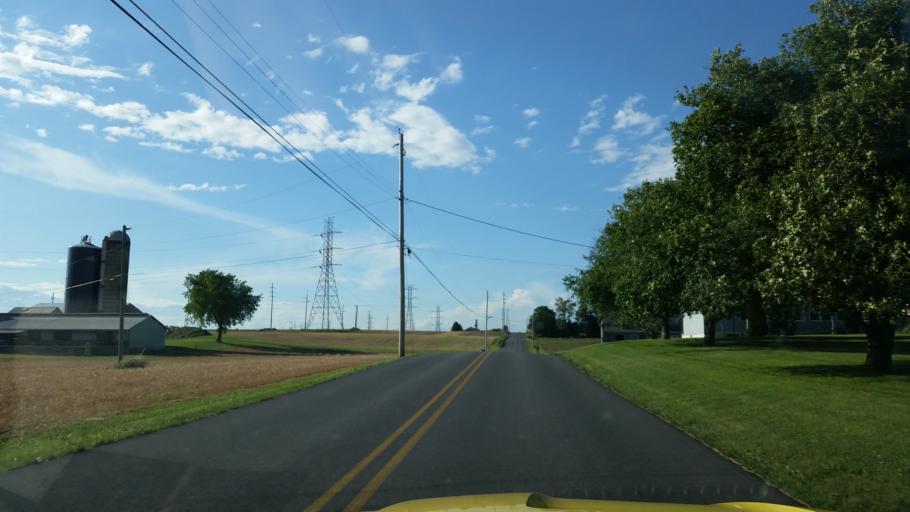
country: US
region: Pennsylvania
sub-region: Lebanon County
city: Avon
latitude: 40.3369
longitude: -76.3622
